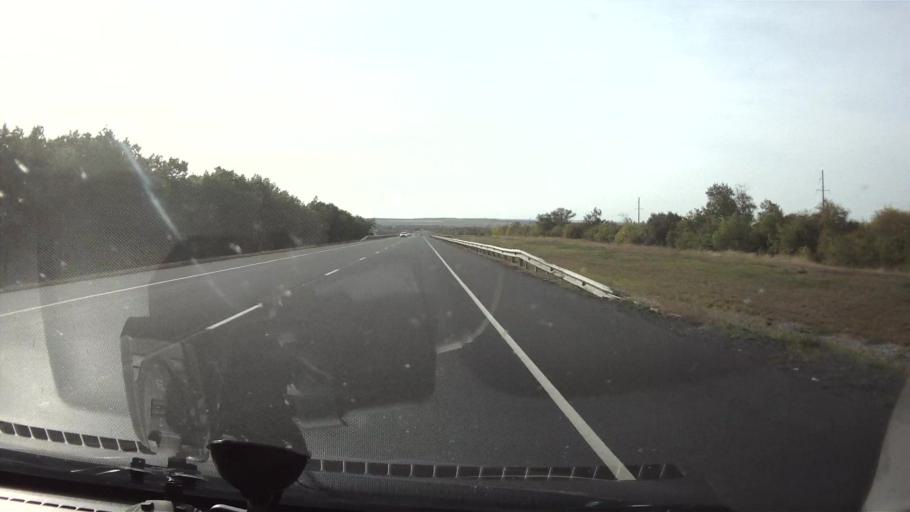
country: RU
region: Saratov
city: Yelshanka
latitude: 51.8264
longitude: 46.2762
